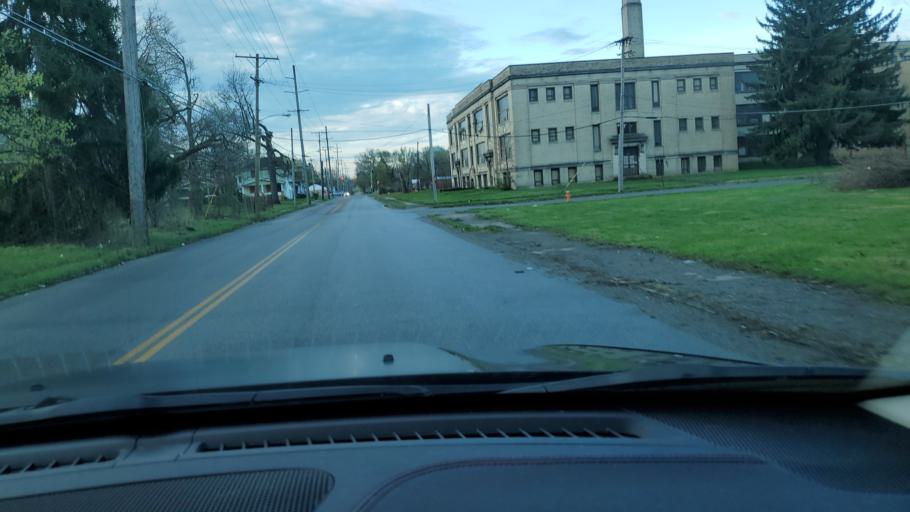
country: US
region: Ohio
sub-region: Mahoning County
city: Youngstown
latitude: 41.0747
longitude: -80.6640
